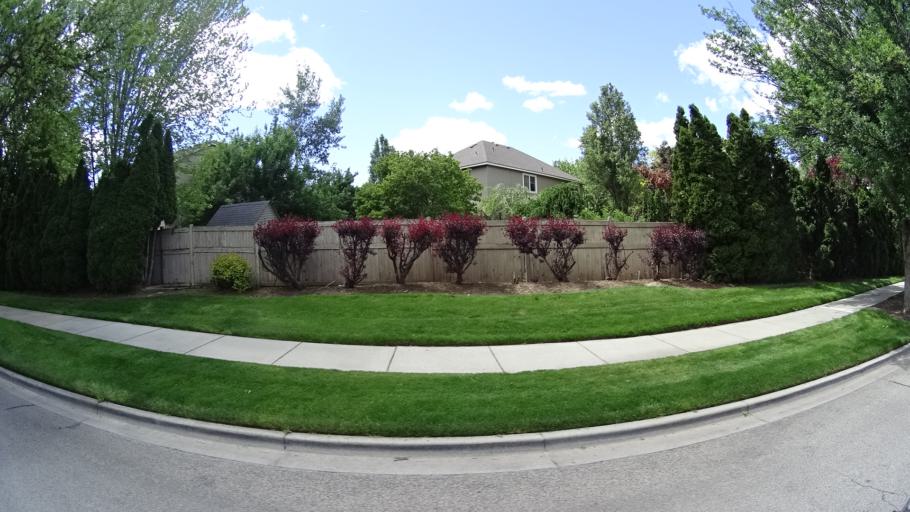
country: US
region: Idaho
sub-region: Ada County
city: Eagle
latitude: 43.6608
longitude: -116.3461
